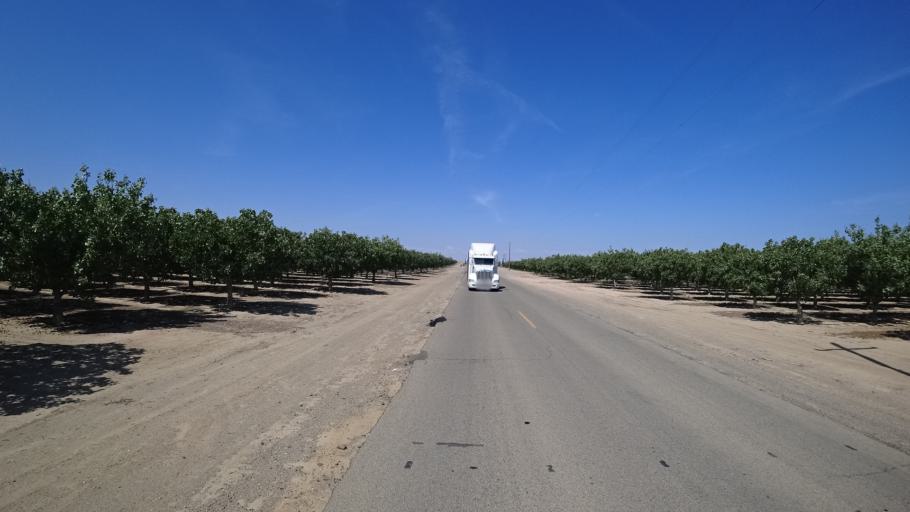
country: US
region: California
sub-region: Kings County
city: Kettleman City
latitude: 36.0724
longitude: -120.0163
